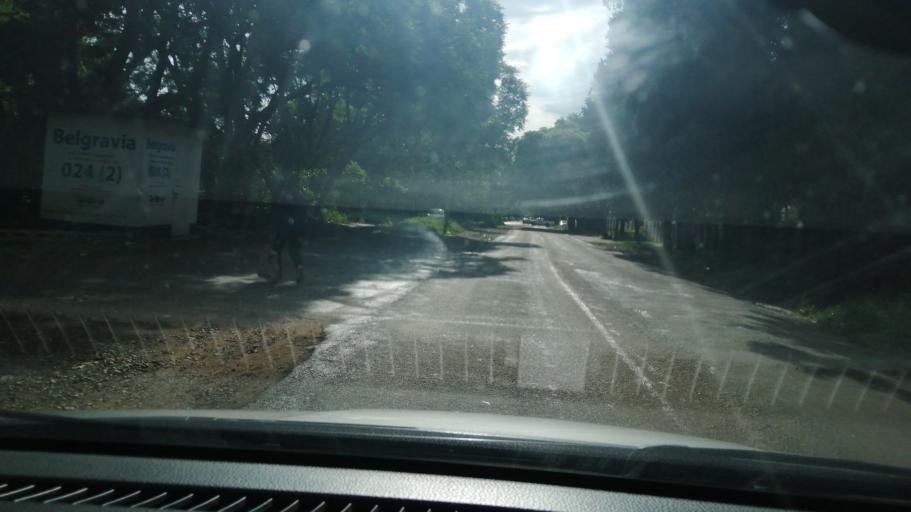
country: ZW
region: Harare
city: Harare
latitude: -17.8070
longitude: 31.0420
